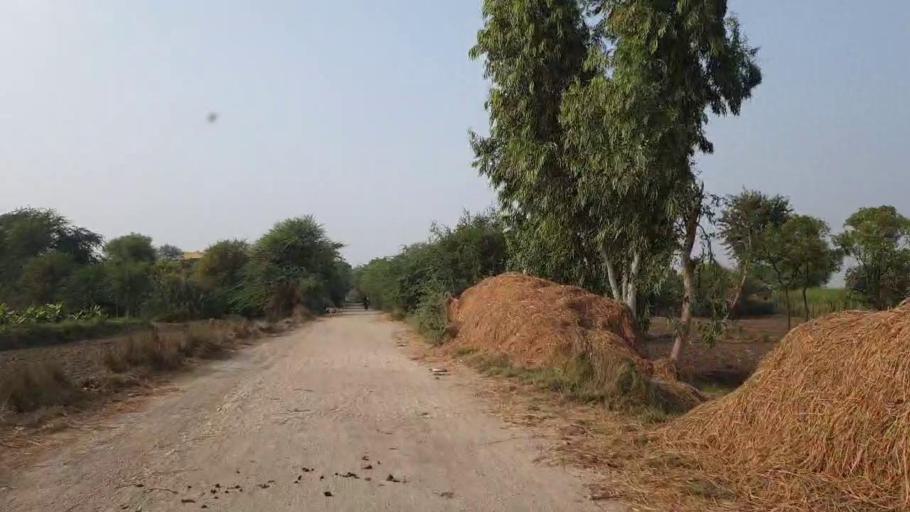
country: PK
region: Sindh
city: Tando Muhammad Khan
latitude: 25.0859
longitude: 68.5841
